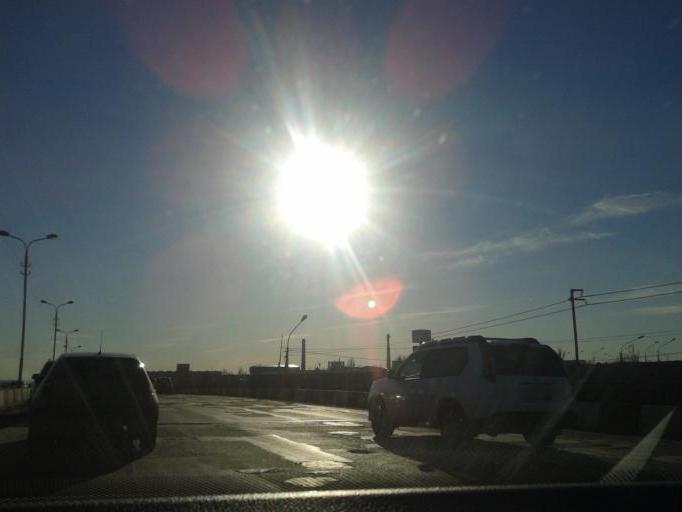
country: RU
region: Volgograd
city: Volgograd
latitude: 48.7541
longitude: 44.4825
